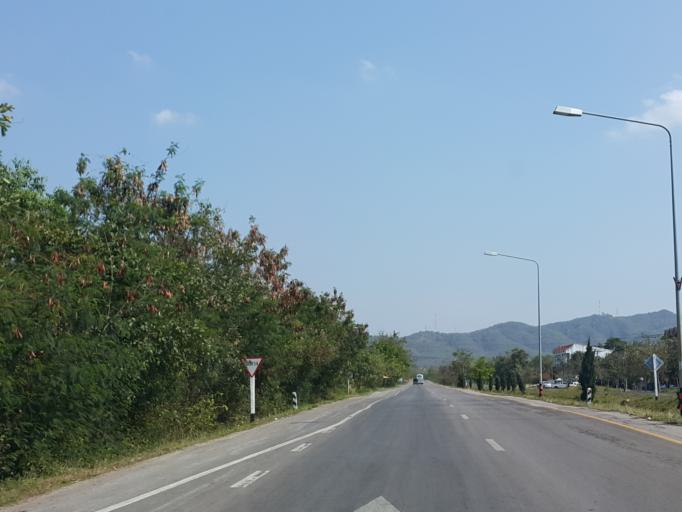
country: TH
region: Lampang
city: Lampang
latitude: 18.2711
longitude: 99.5260
